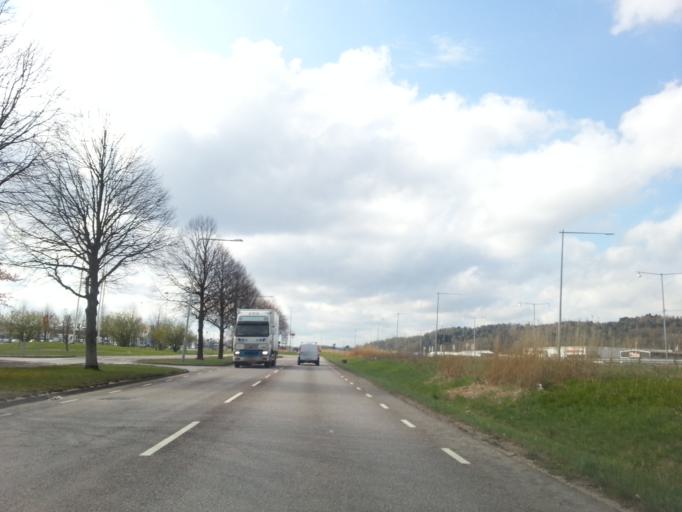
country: SE
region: Vaestra Goetaland
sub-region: Goteborg
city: Hammarkullen
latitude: 57.7768
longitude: 11.9988
